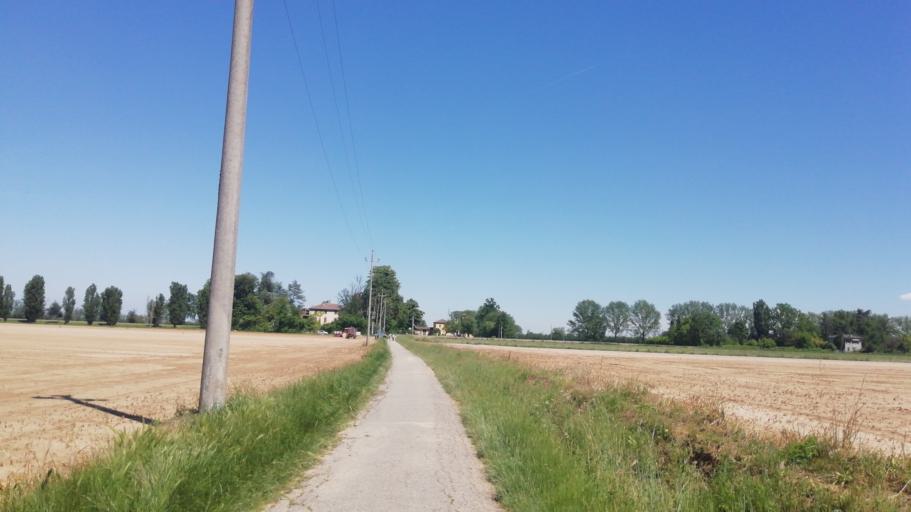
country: IT
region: Emilia-Romagna
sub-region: Provincia di Piacenza
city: Borgonovo Valtidone
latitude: 45.0015
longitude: 9.4536
